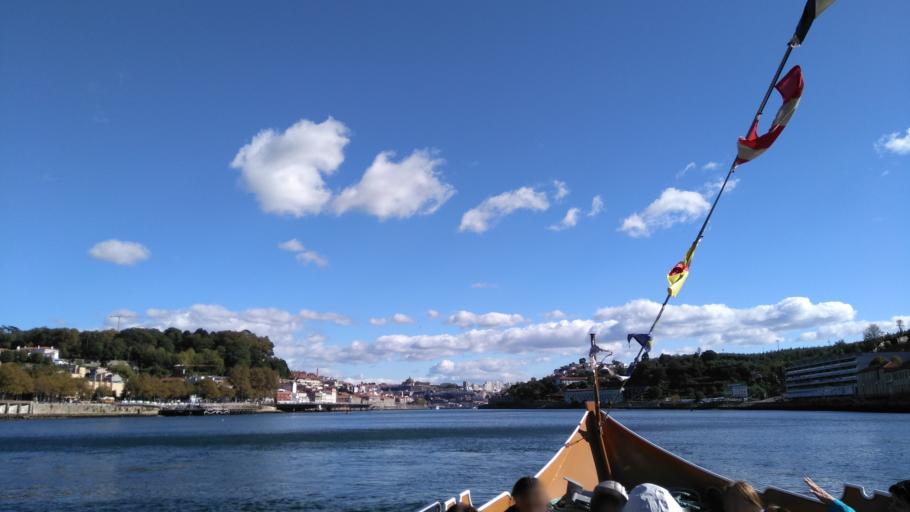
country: PT
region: Porto
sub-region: Vila Nova de Gaia
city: Vila Nova de Gaia
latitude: 41.1469
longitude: -8.6377
